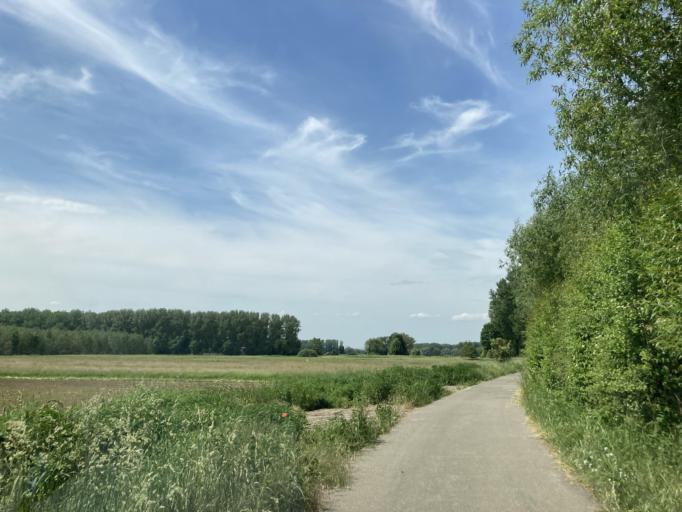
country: DE
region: Baden-Wuerttemberg
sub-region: Karlsruhe Region
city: Graben-Neudorf
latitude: 49.1700
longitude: 8.4701
